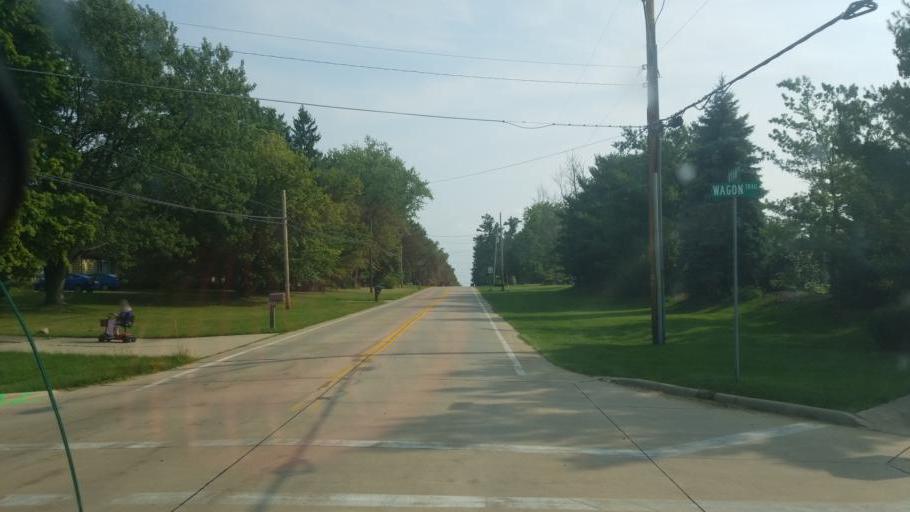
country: US
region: Ohio
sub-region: Medina County
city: Medina
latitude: 41.1132
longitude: -81.8840
